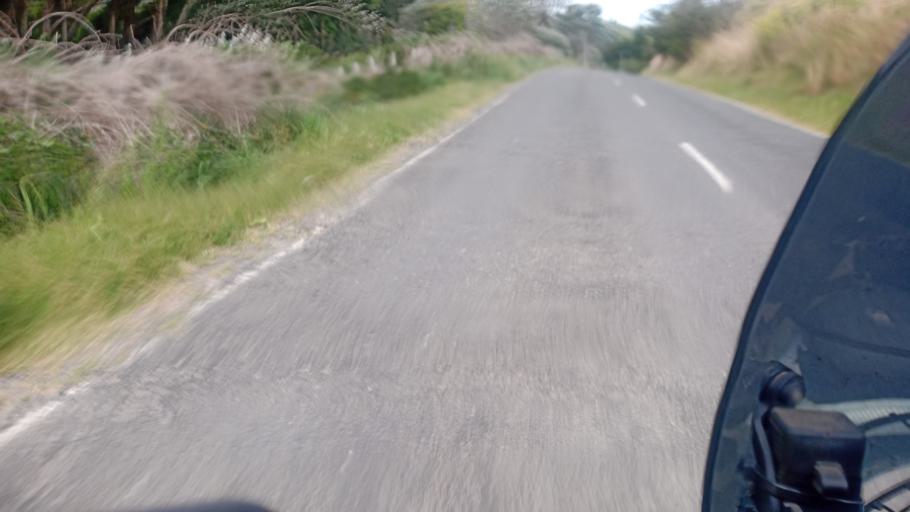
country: NZ
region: Gisborne
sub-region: Gisborne District
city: Gisborne
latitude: -38.5643
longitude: 177.9004
